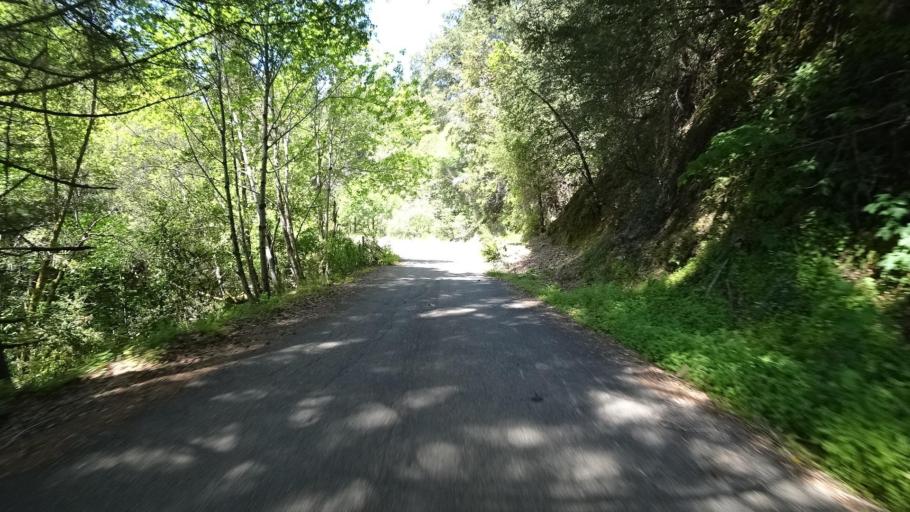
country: US
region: California
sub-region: Humboldt County
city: Redway
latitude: 40.1966
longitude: -123.5561
